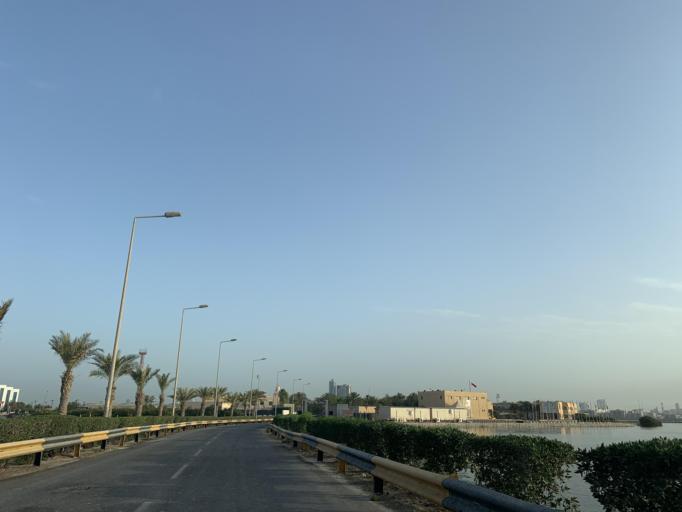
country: BH
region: Manama
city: Manama
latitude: 26.1876
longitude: 50.5858
